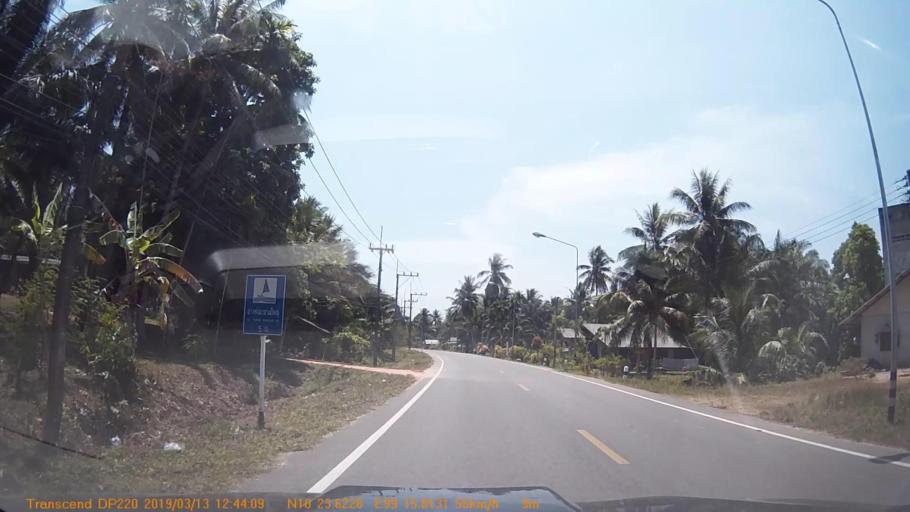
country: TH
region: Chumphon
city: Chumphon
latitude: 10.3935
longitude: 99.2634
